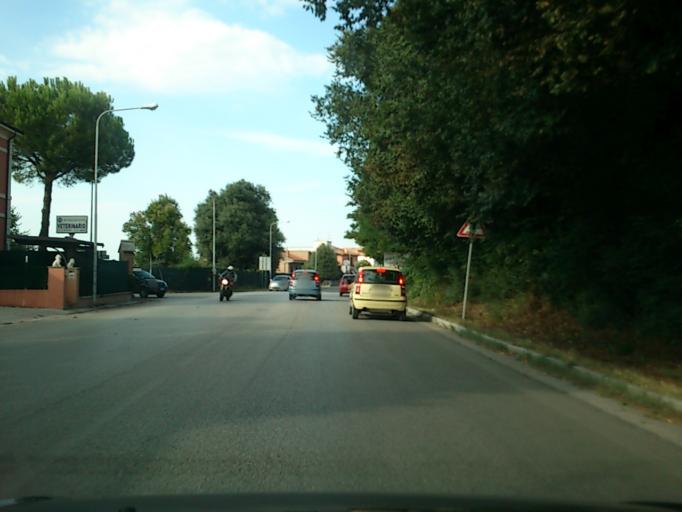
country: IT
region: The Marches
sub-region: Provincia di Pesaro e Urbino
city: Centinarola
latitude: 43.8257
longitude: 12.9938
